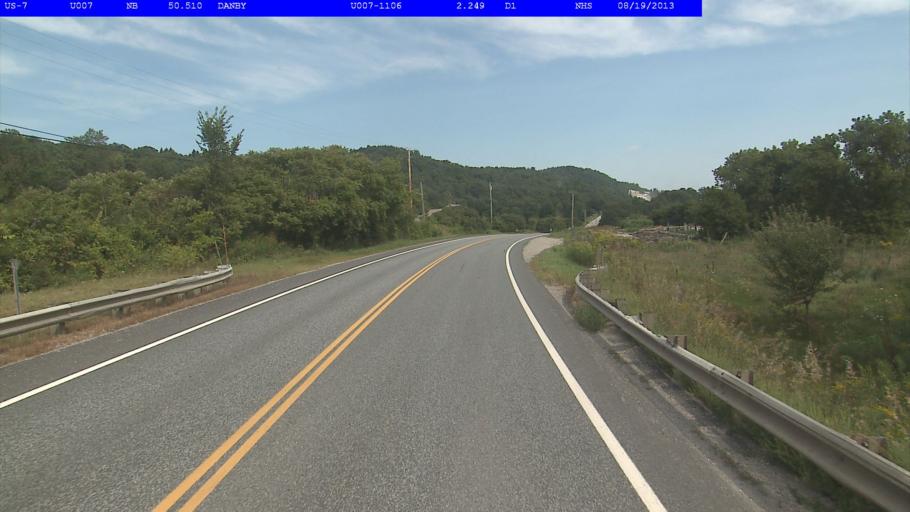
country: US
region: Vermont
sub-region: Rutland County
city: West Rutland
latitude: 43.3942
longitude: -72.9987
